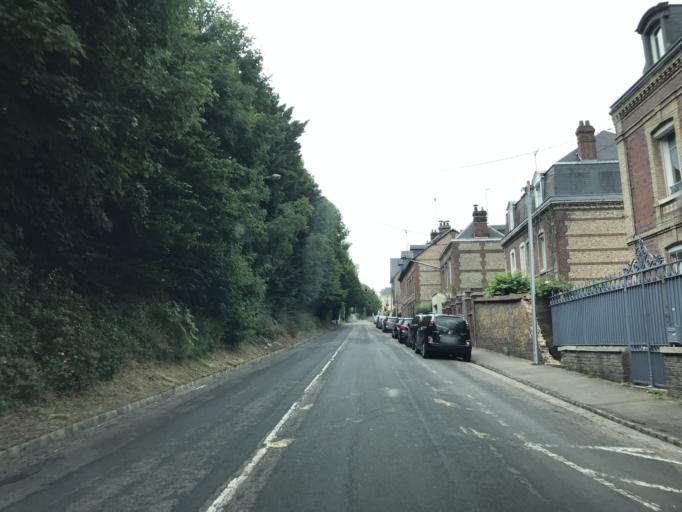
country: FR
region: Haute-Normandie
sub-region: Departement de la Seine-Maritime
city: Mont-Saint-Aignan
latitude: 49.4578
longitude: 1.0842
